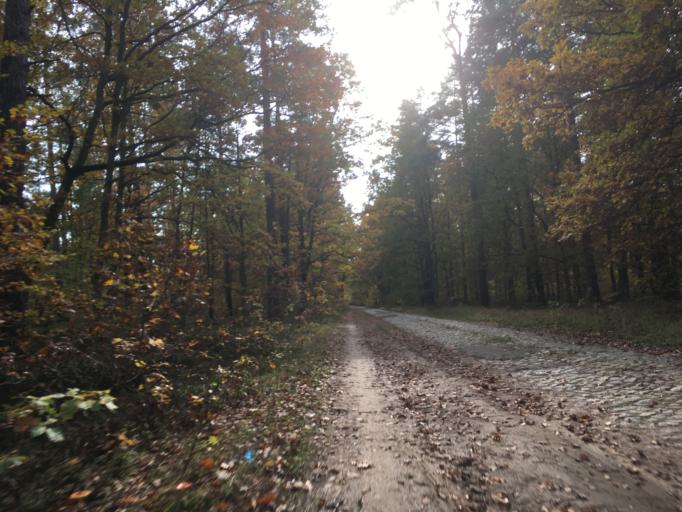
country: DE
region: Brandenburg
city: Liebenwalde
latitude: 52.9794
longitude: 13.4814
